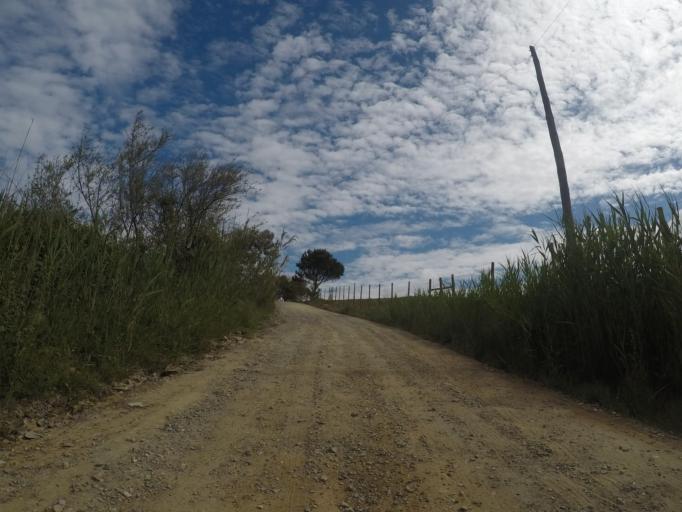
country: PT
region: Beja
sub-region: Odemira
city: Sao Teotonio
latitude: 37.5017
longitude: -8.7885
